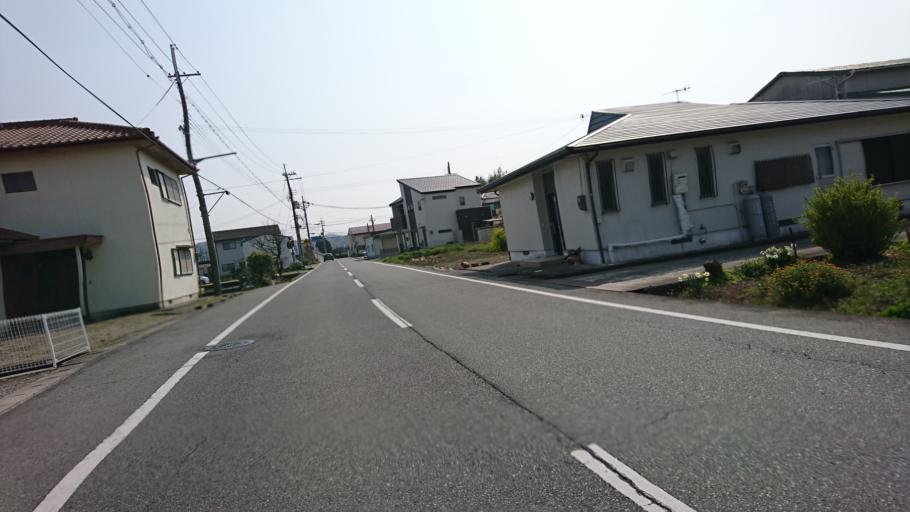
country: JP
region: Hyogo
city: Ono
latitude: 34.8542
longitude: 134.9113
